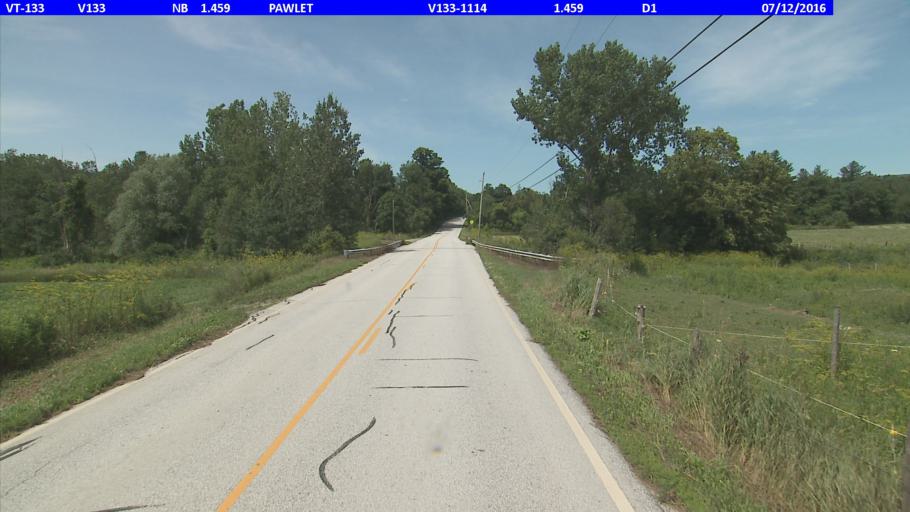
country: US
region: New York
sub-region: Washington County
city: Granville
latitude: 43.3539
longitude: -73.1528
